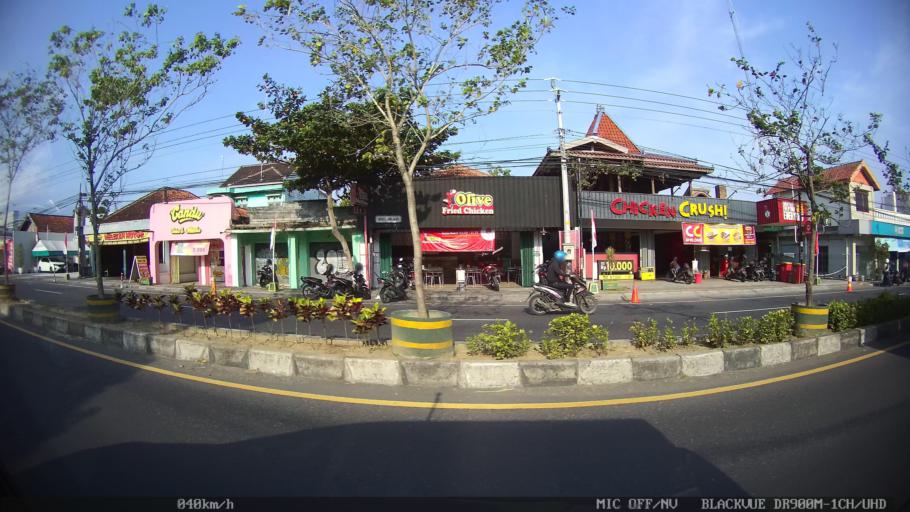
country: ID
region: Daerah Istimewa Yogyakarta
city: Bantul
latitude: -7.8759
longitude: 110.3353
